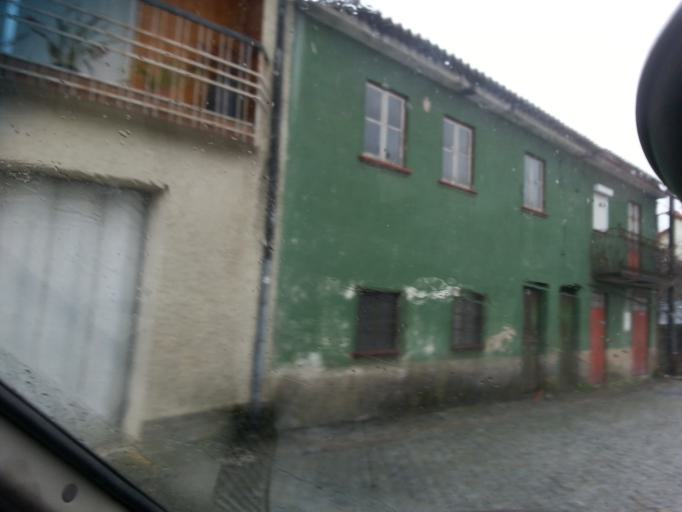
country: PT
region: Viseu
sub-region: Viseu
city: Rio de Loba
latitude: 40.6645
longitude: -7.8784
